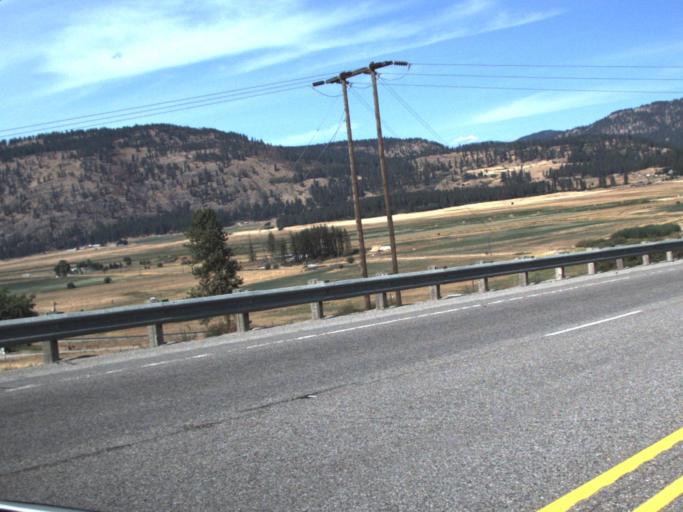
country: US
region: Washington
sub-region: Stevens County
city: Chewelah
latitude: 48.2049
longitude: -117.7144
